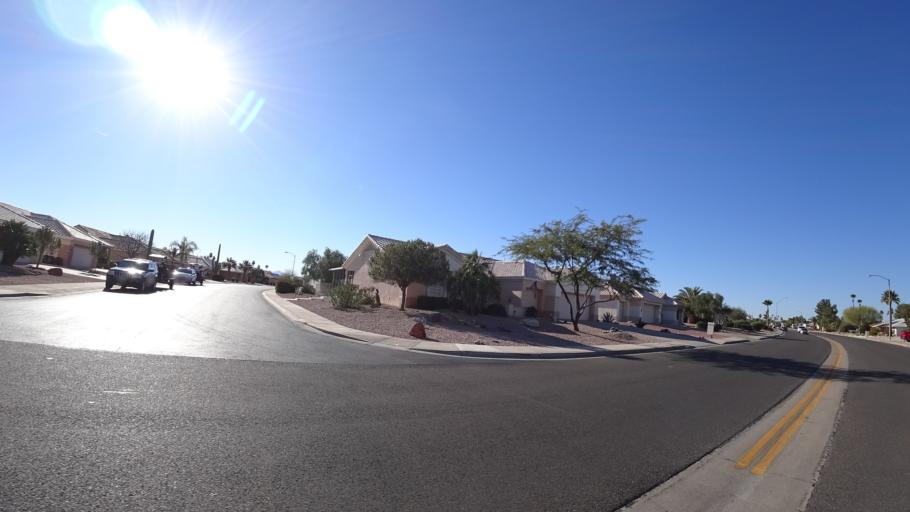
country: US
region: Arizona
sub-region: Maricopa County
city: Sun City West
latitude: 33.6682
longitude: -112.3412
